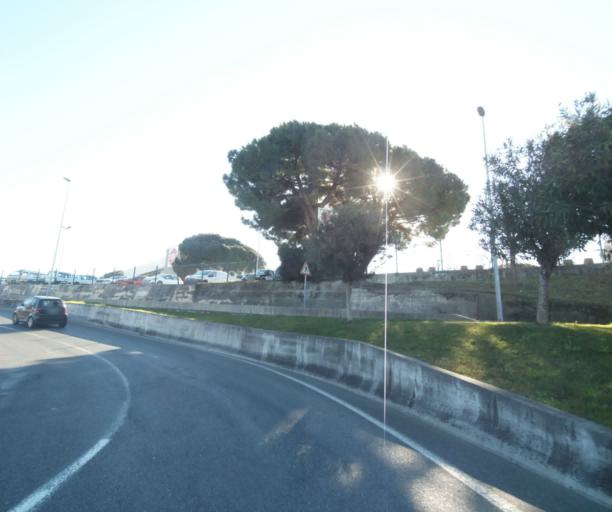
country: FR
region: Provence-Alpes-Cote d'Azur
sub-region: Departement des Alpes-Maritimes
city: Antibes
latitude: 43.5774
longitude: 7.1056
